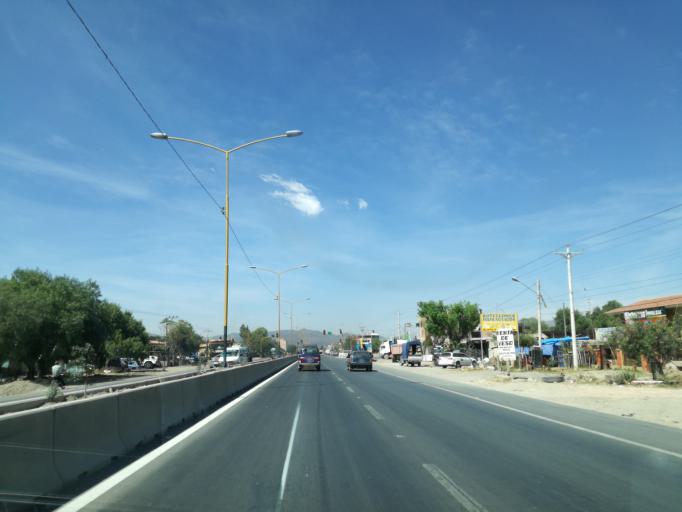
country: BO
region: Cochabamba
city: Sipe Sipe
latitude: -17.4181
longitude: -66.3329
